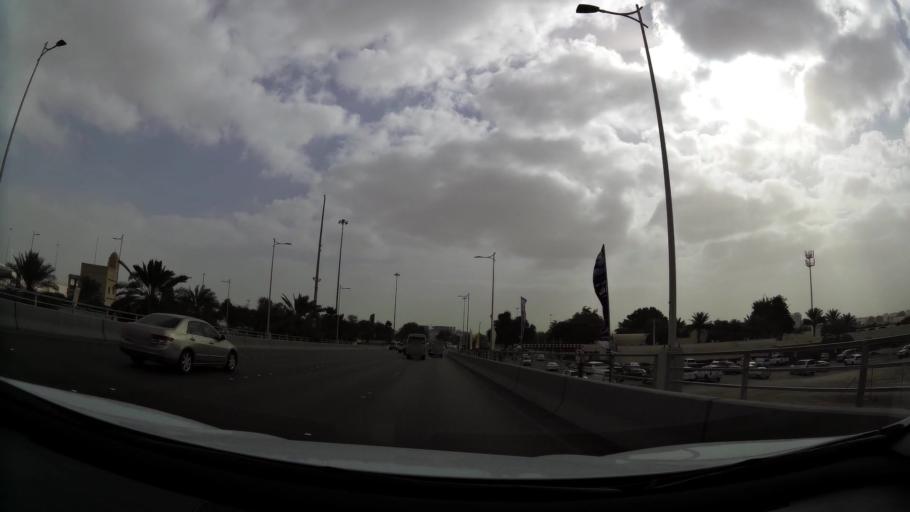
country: AE
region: Abu Dhabi
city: Abu Dhabi
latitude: 24.4204
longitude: 54.4879
